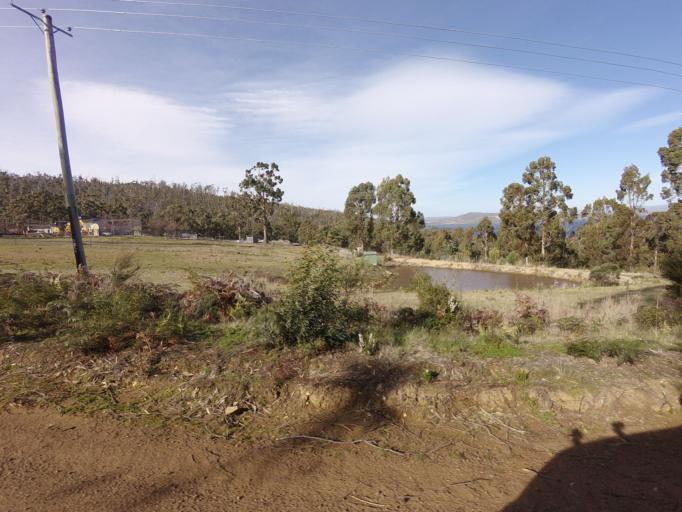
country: AU
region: Tasmania
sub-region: Kingborough
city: Kettering
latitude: -43.0933
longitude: 147.2641
